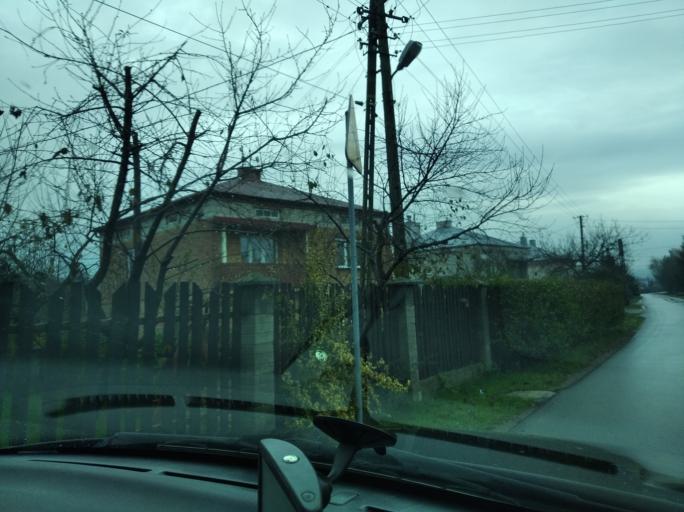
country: PL
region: Subcarpathian Voivodeship
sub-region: Powiat strzyzowski
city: Czudec
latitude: 49.9434
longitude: 21.8409
